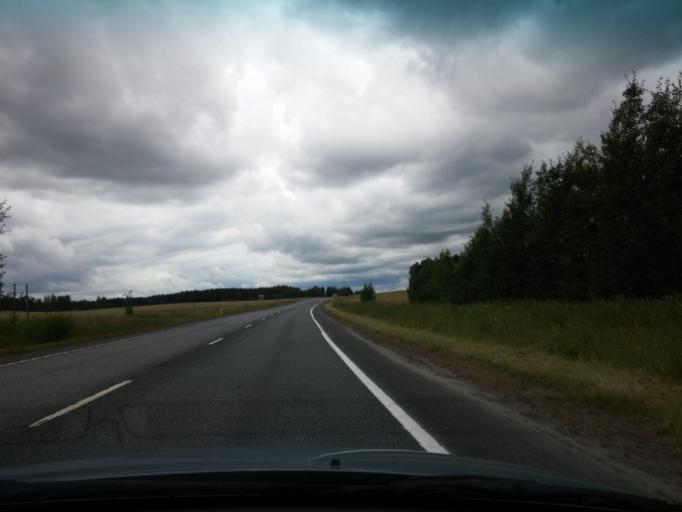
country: FI
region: Uusimaa
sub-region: Porvoo
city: Porvoo
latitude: 60.3975
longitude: 25.5990
